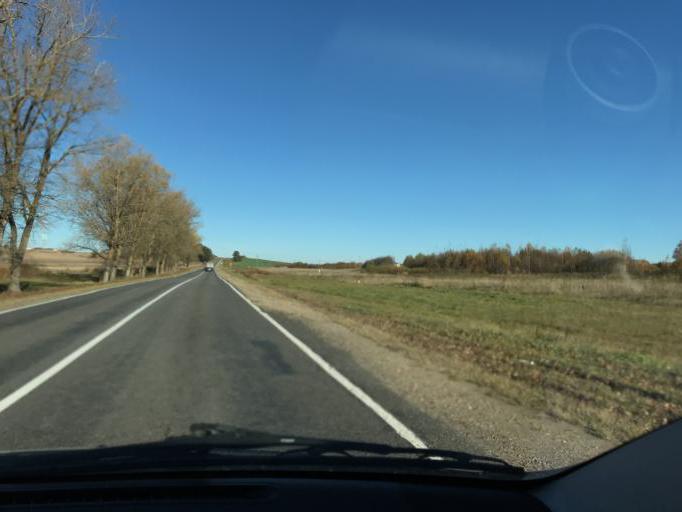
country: BY
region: Vitebsk
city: Lyepyel'
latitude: 54.9976
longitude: 28.7374
